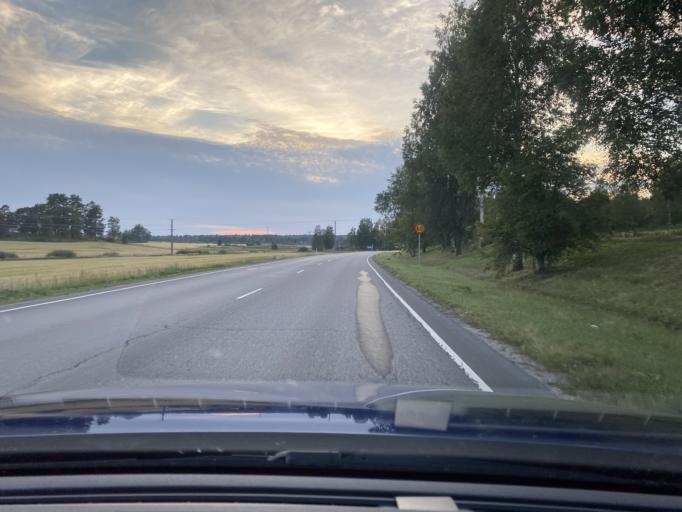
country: FI
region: Satakunta
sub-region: Pohjois-Satakunta
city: Kankaanpaeae
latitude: 61.7847
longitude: 22.4254
